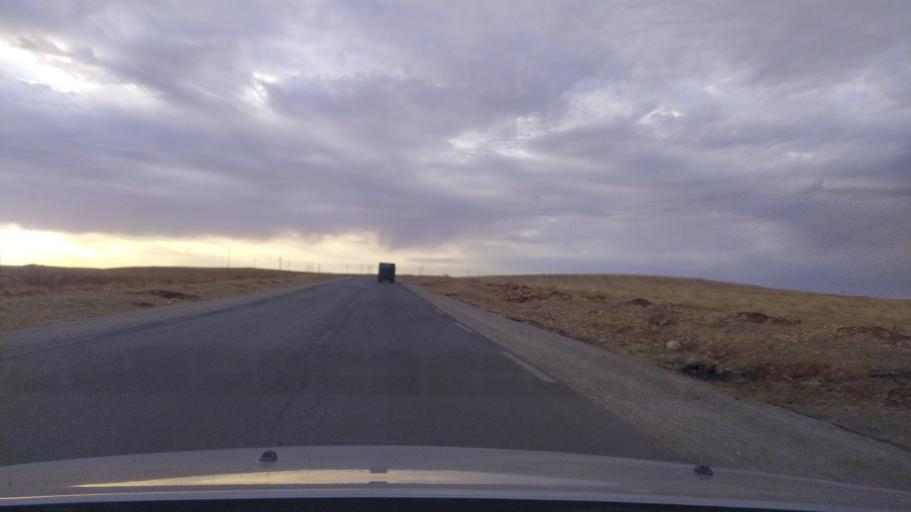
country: DZ
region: Tiaret
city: Frenda
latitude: 34.9862
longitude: 1.1378
